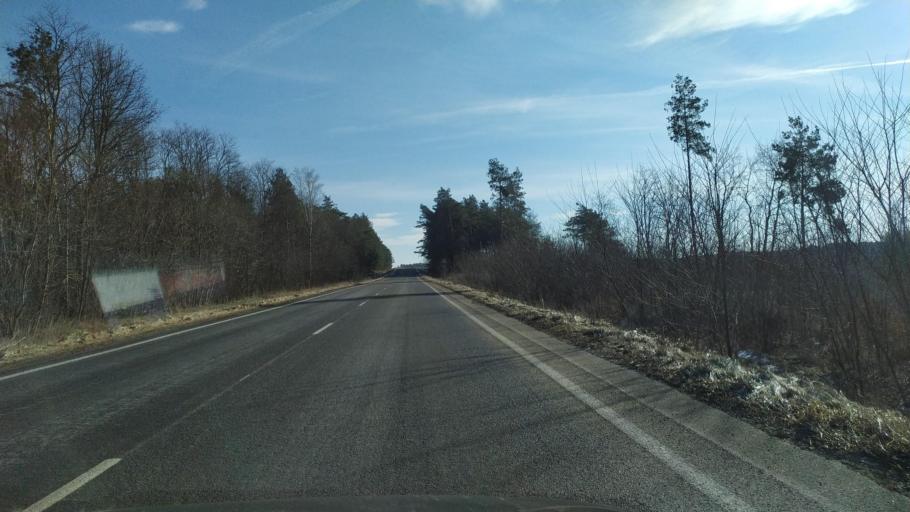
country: BY
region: Brest
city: Kamyanyets
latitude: 52.3993
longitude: 23.9049
